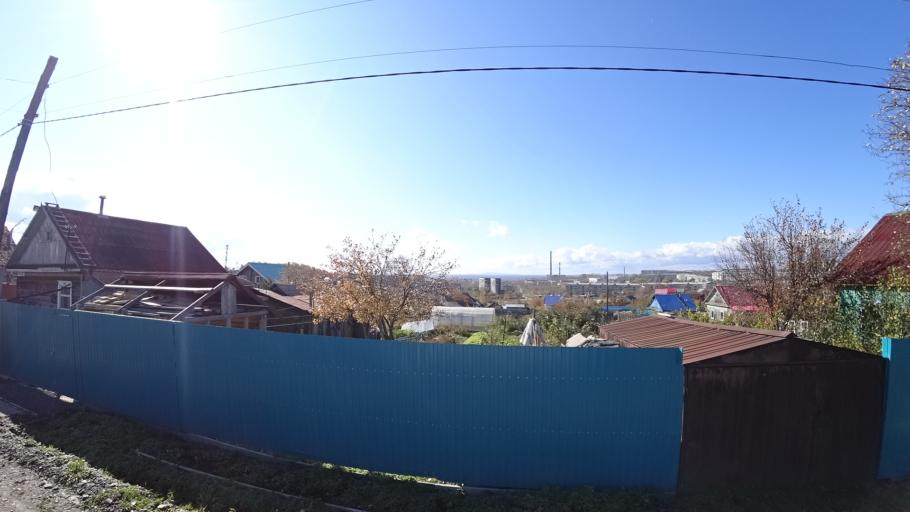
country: RU
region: Khabarovsk Krai
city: Amursk
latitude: 50.2373
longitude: 136.9184
